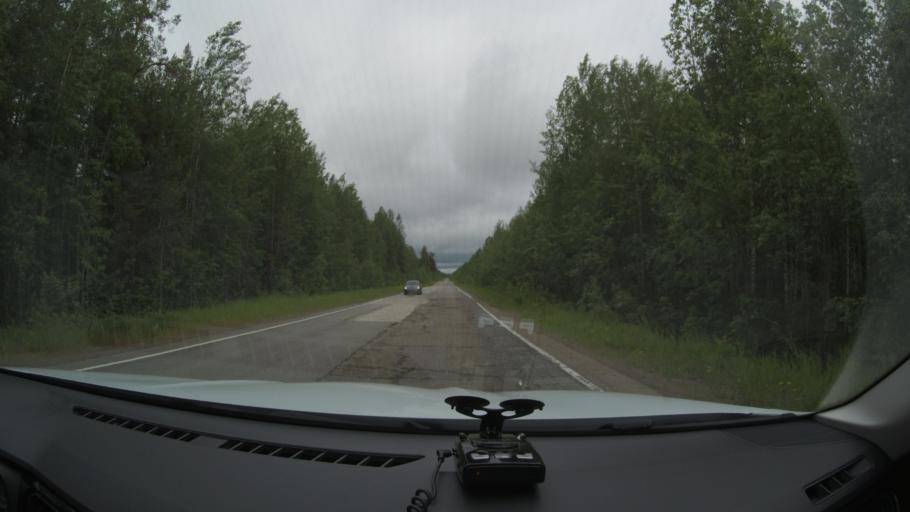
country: RU
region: Komi Republic
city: Nizhniy Odes
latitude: 63.6580
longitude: 54.6745
